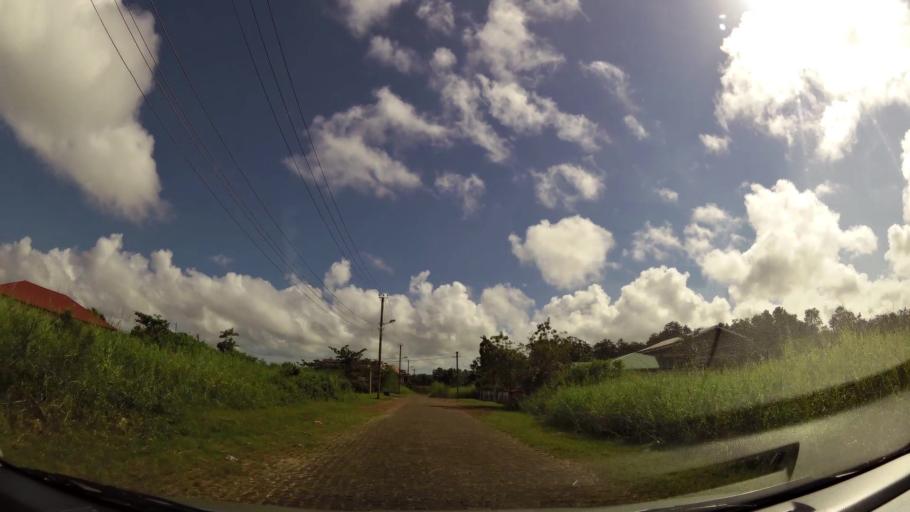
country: SR
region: Commewijne
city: Nieuw Amsterdam
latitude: 5.8790
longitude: -55.1143
